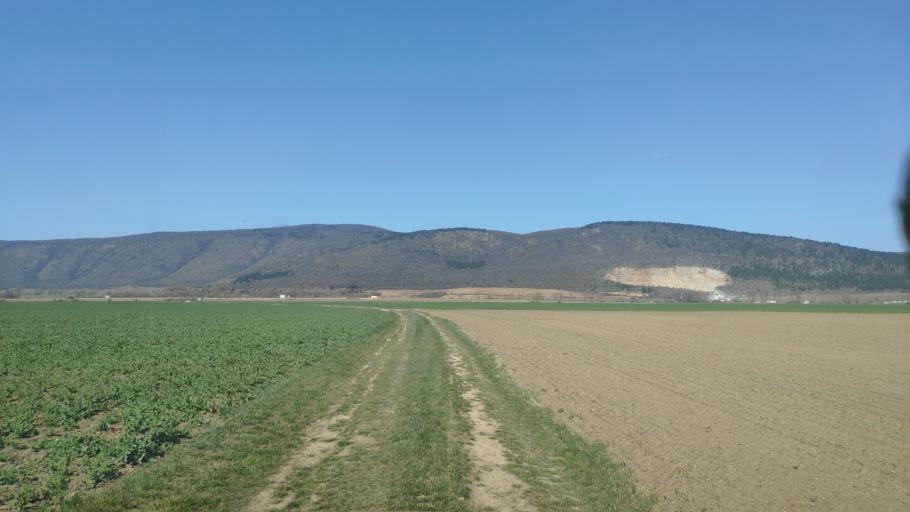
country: SK
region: Kosicky
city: Moldava nad Bodvou
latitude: 48.6000
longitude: 20.9315
